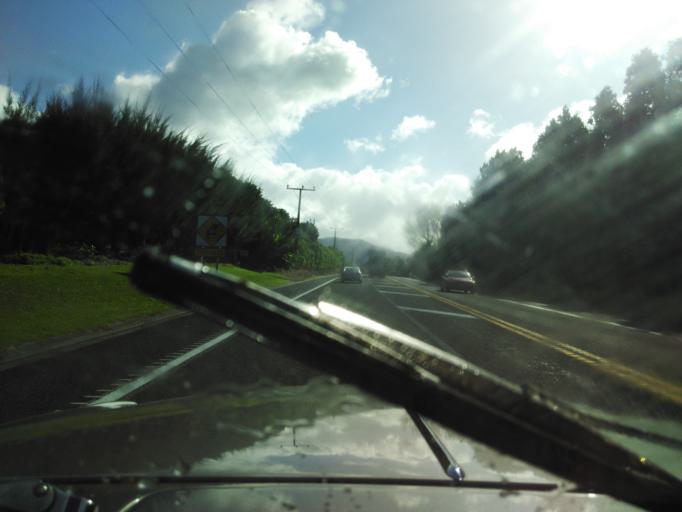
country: NZ
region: Bay of Plenty
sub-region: Western Bay of Plenty District
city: Katikati
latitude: -37.5211
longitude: 175.9200
